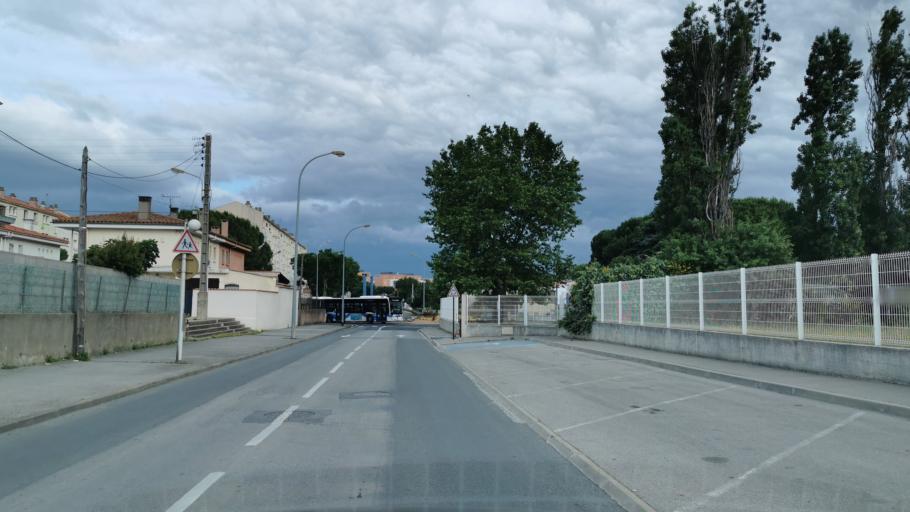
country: FR
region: Languedoc-Roussillon
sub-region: Departement de l'Aude
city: Narbonne
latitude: 43.1938
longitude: 3.0182
